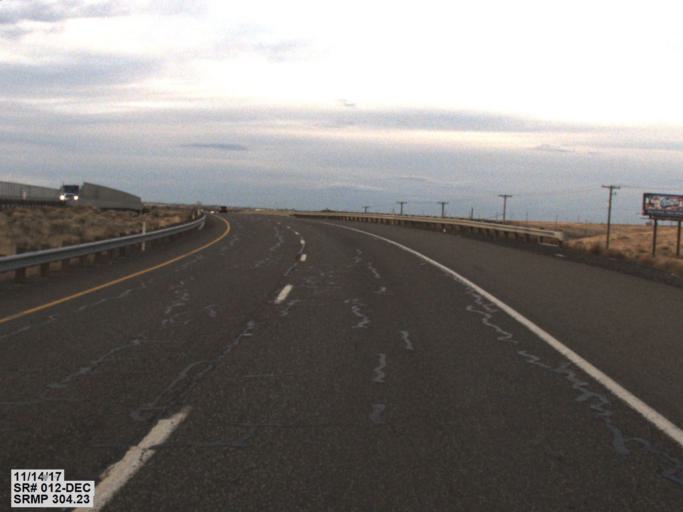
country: US
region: Washington
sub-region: Benton County
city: Finley
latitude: 46.1045
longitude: -118.9135
